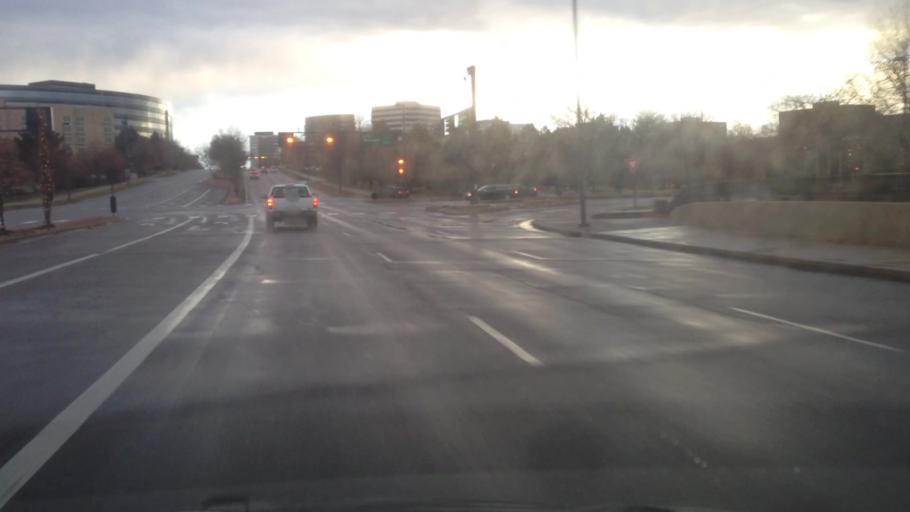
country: US
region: Colorado
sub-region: Arapahoe County
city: Castlewood
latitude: 39.6242
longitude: -104.8888
